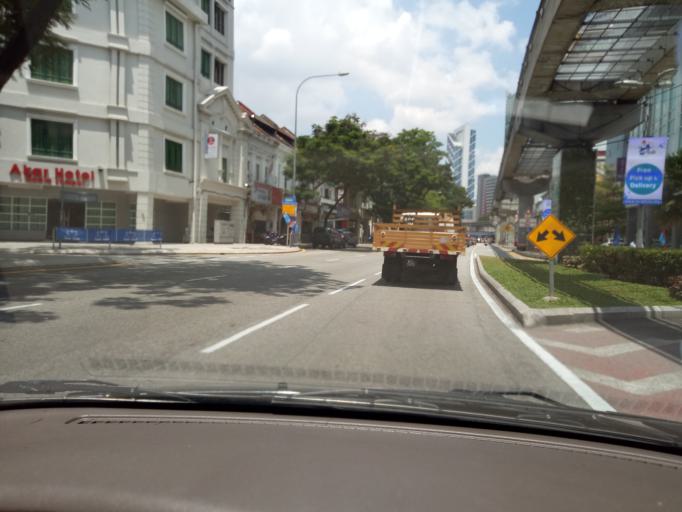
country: MY
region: Kuala Lumpur
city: Kuala Lumpur
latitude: 3.1626
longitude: 101.6979
